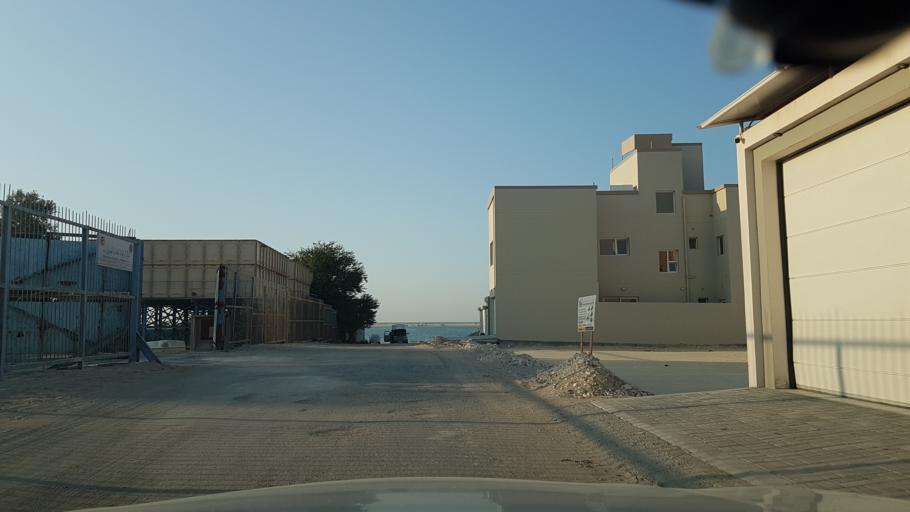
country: BH
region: Manama
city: Jidd Hafs
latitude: 26.2347
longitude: 50.5057
